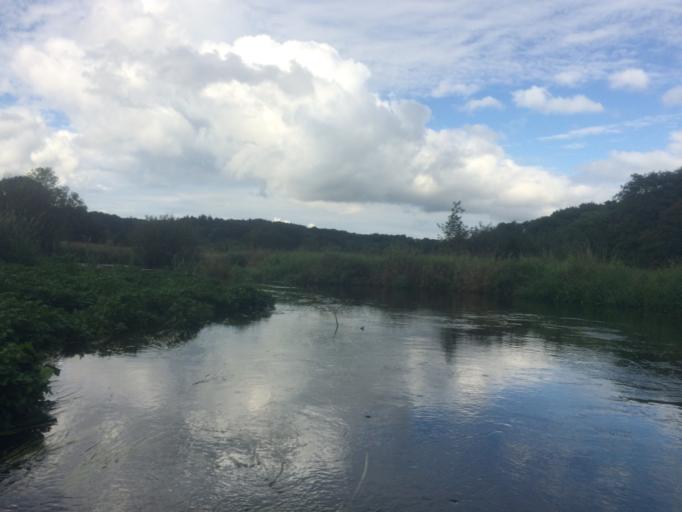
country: DK
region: South Denmark
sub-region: Vejle Kommune
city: Egtved
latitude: 55.6588
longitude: 9.3159
